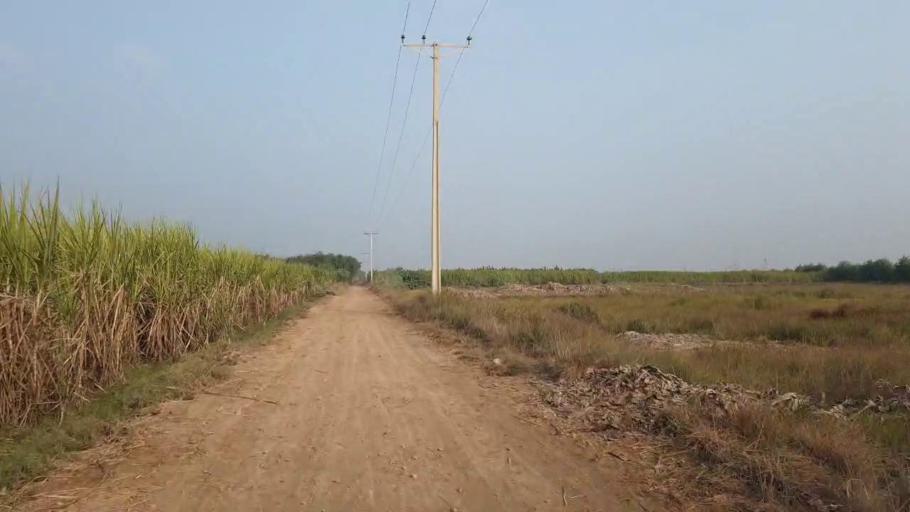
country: PK
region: Sindh
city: Tando Muhammad Khan
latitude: 25.1522
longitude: 68.5874
